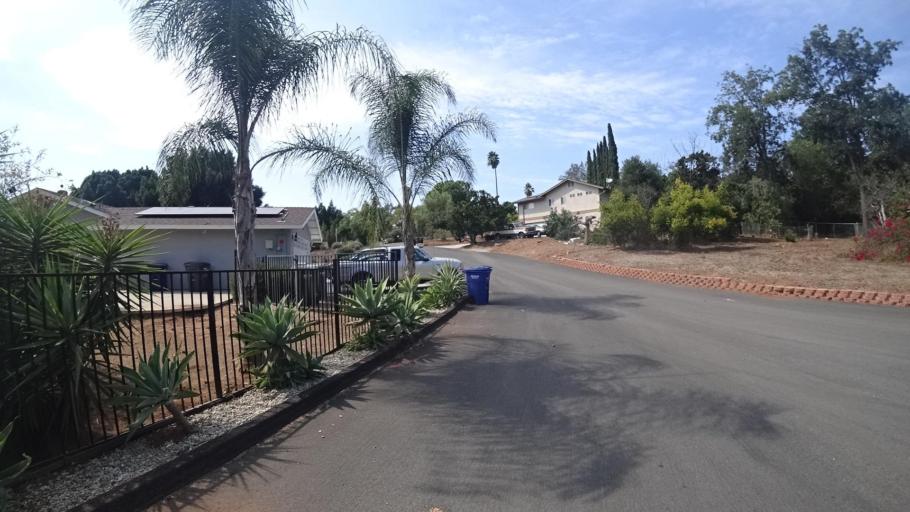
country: US
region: California
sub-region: San Diego County
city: Escondido
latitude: 33.1209
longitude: -117.0528
